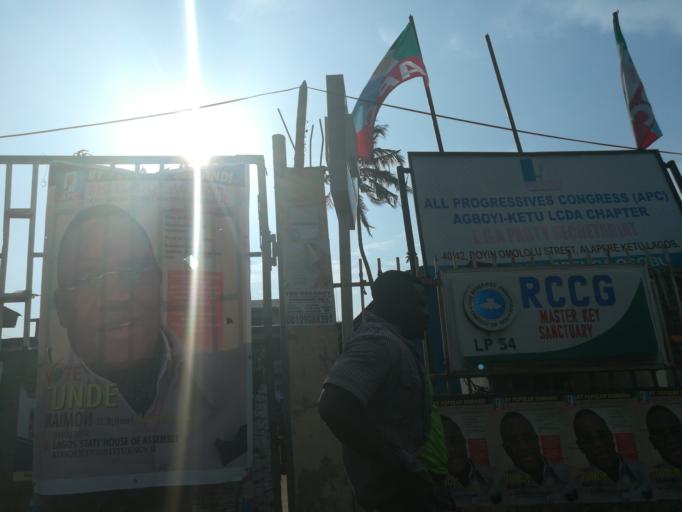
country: NG
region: Lagos
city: Ojota
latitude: 6.5933
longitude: 3.3952
